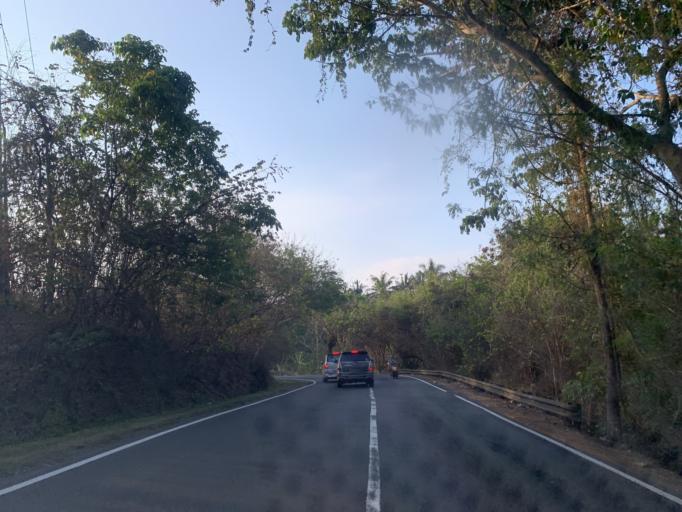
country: ID
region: Bali
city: Banjar Delodrurung
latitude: -8.5048
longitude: 114.9744
